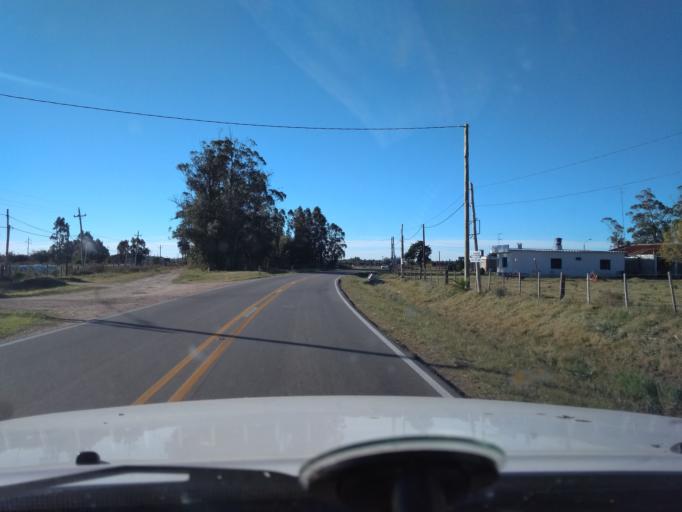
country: UY
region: Canelones
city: Santa Rosa
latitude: -34.5111
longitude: -56.0539
